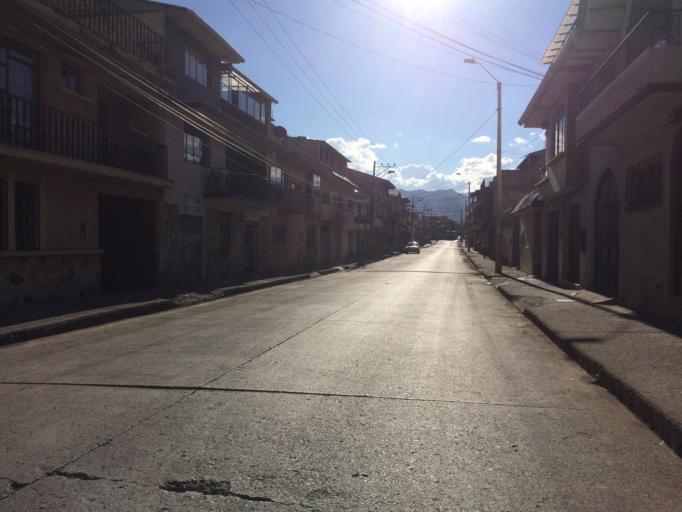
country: EC
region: Azuay
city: Cuenca
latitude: -2.8912
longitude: -79.0144
